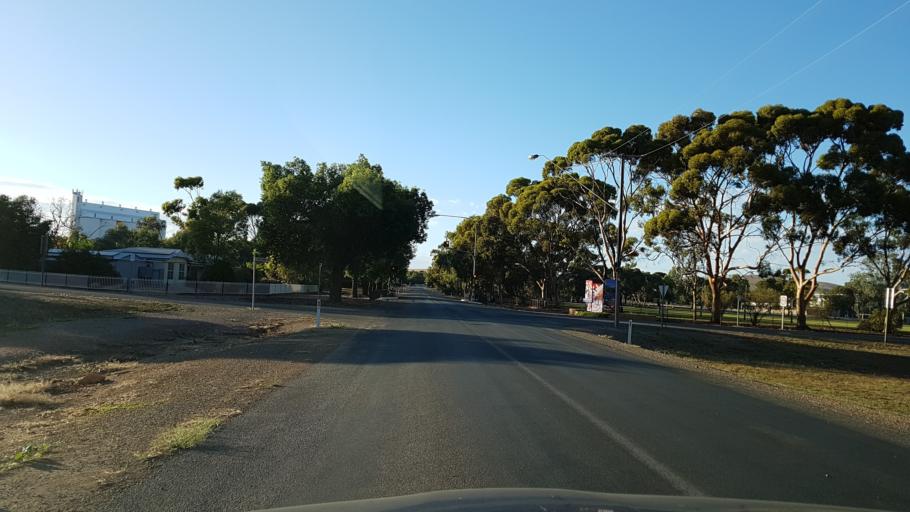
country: AU
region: South Australia
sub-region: Port Pirie City and Dists
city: Crystal Brook
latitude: -33.2720
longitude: 138.3532
